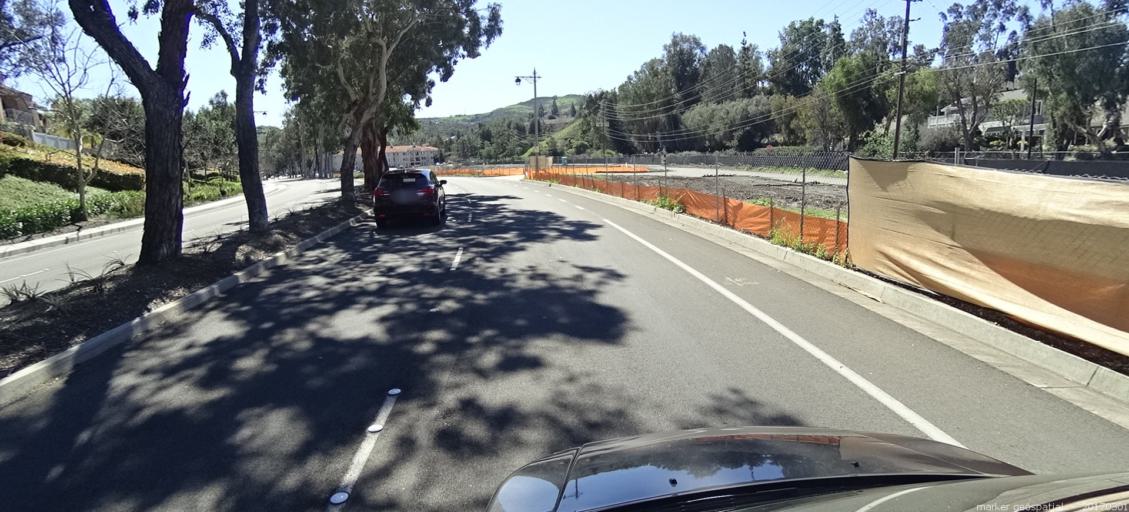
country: US
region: California
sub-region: Orange County
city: Villa Park
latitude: 33.8488
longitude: -117.7788
